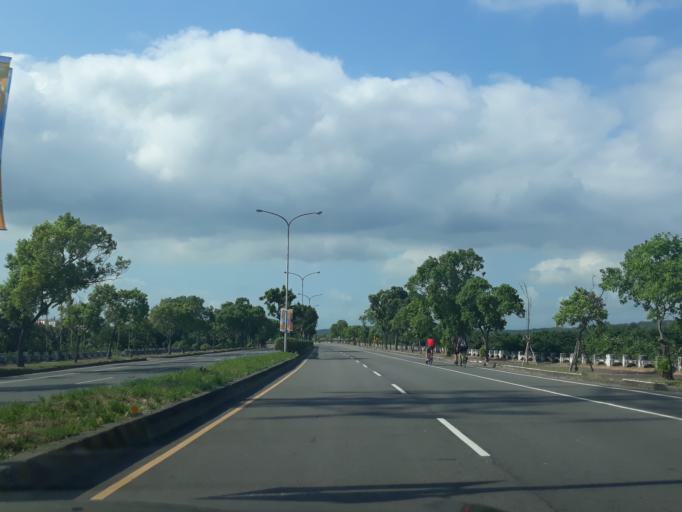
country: TW
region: Taiwan
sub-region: Miaoli
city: Miaoli
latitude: 24.5824
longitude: 120.8430
